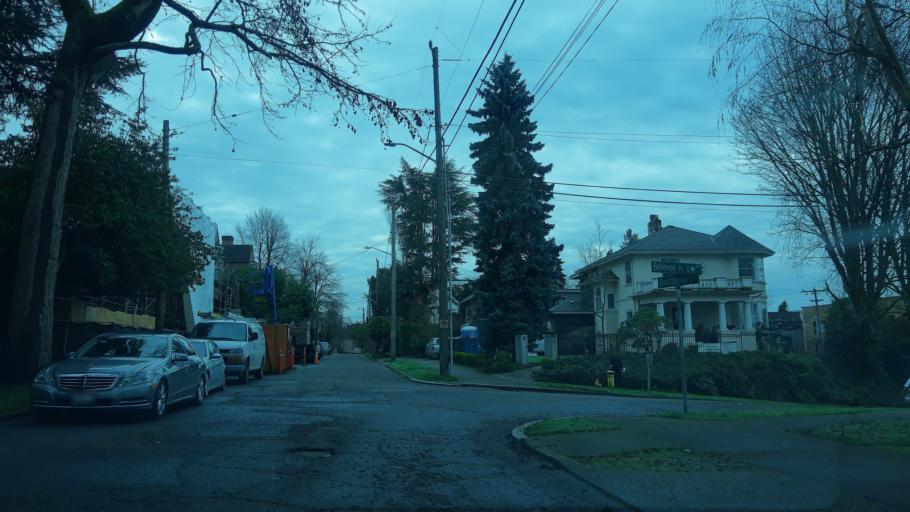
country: US
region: Washington
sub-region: King County
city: Seattle
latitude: 47.6282
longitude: -122.3236
